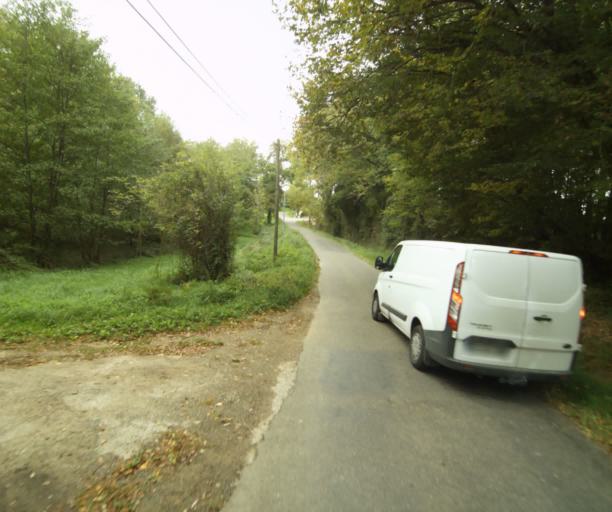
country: FR
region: Midi-Pyrenees
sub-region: Departement du Gers
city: Eauze
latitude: 43.8994
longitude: 0.1005
